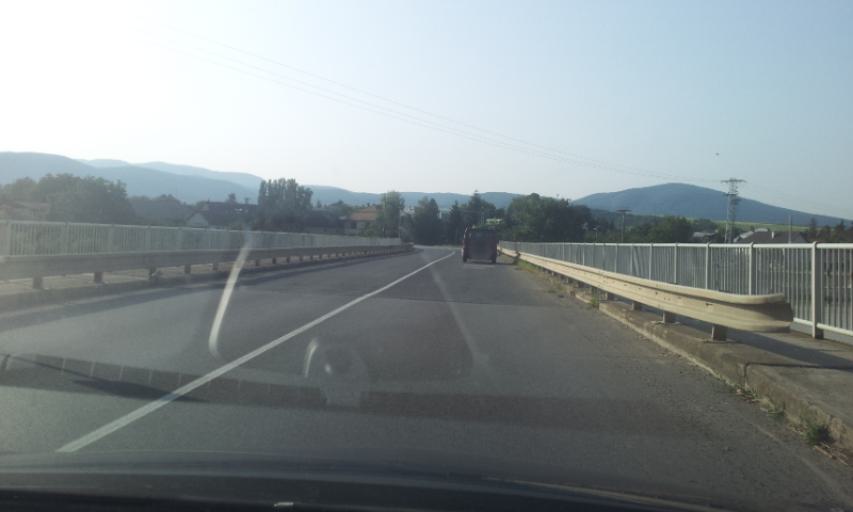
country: SK
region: Kosicky
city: Kosice
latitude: 48.6053
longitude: 21.3435
